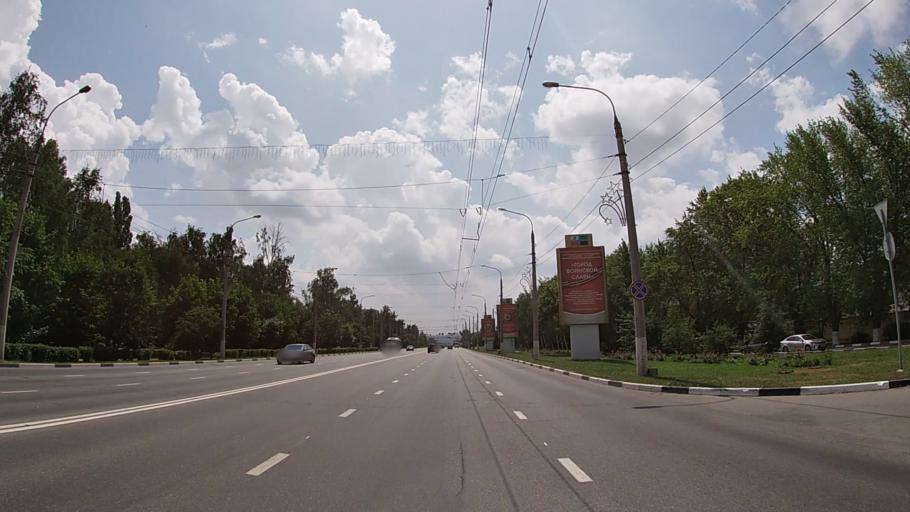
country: RU
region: Belgorod
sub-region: Belgorodskiy Rayon
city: Belgorod
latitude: 50.6266
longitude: 36.5744
